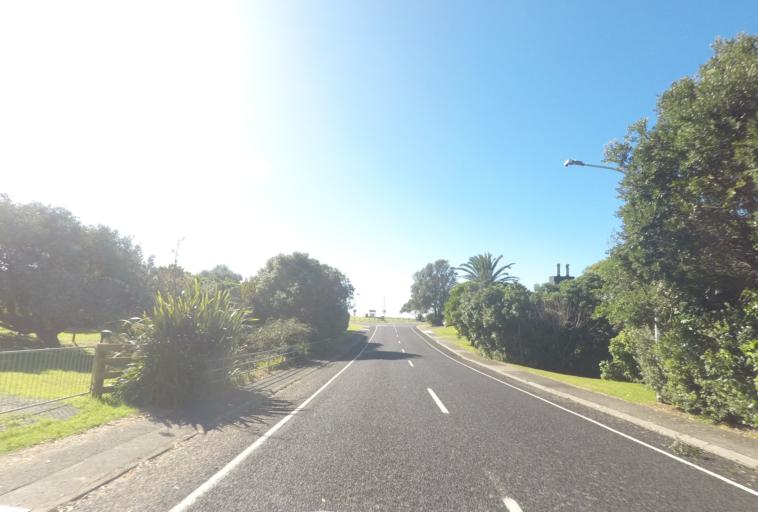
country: NZ
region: Waikato
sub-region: Thames-Coromandel District
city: Whangamata
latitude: -37.2827
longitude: 175.9012
